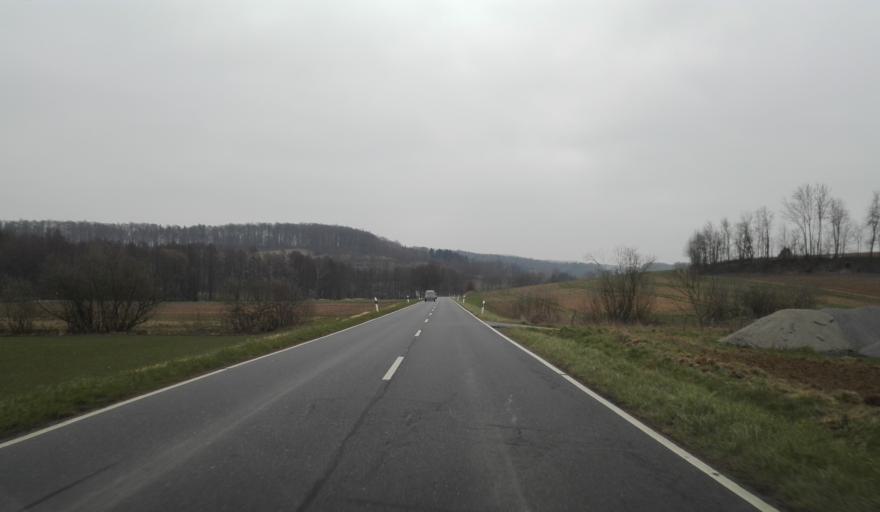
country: DE
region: Hesse
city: Lutzelbach
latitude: 49.7811
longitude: 8.7441
